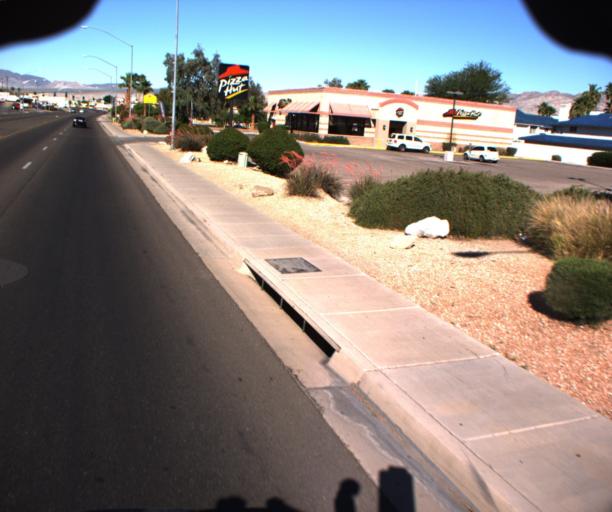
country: US
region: Arizona
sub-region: Mohave County
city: Bullhead City
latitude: 35.1198
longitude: -114.5924
